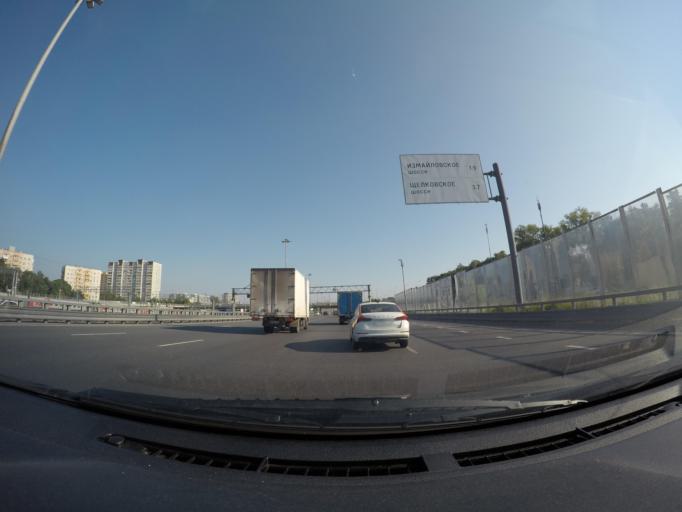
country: RU
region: Moscow
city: Ryazanskiy
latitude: 55.7667
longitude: 37.7479
